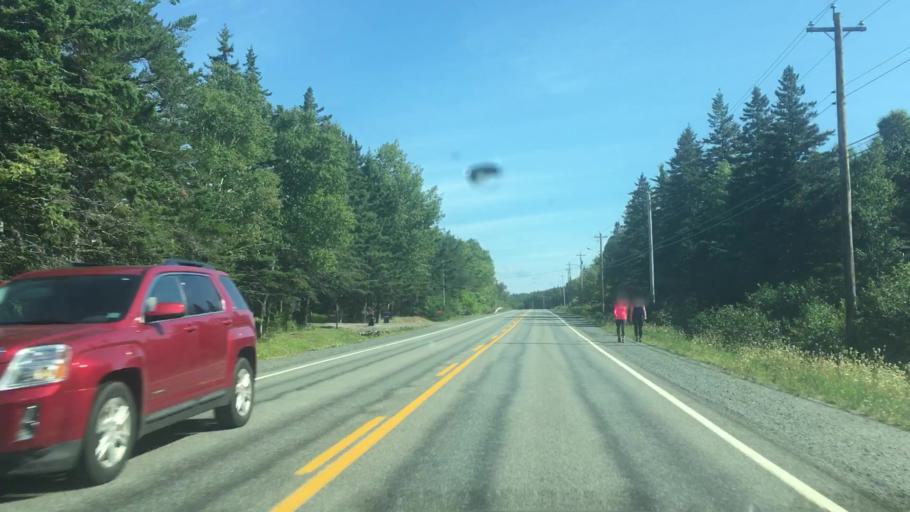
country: CA
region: Nova Scotia
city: Sydney
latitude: 45.9870
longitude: -60.4177
